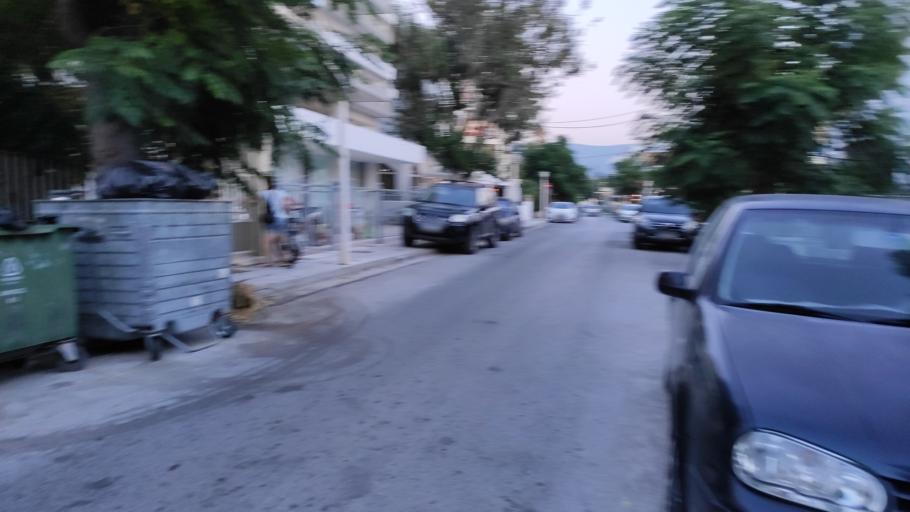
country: GR
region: South Aegean
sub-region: Nomos Dodekanisou
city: Kos
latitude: 36.8990
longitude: 27.2830
